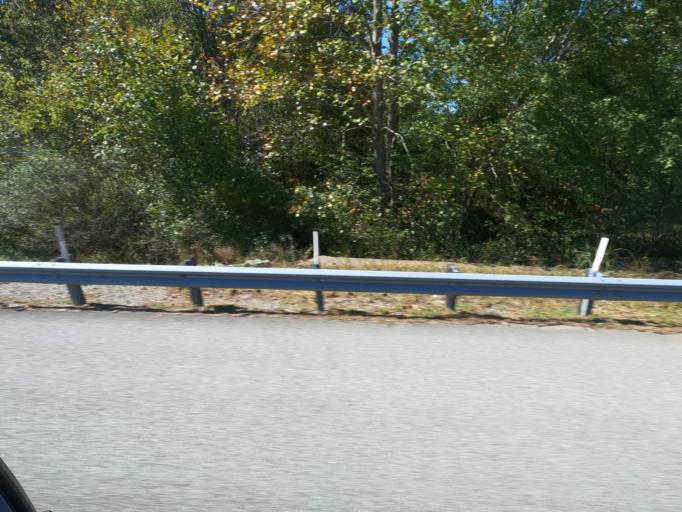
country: US
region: Tennessee
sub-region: Maury County
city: Mount Pleasant
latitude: 35.4139
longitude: -87.2821
